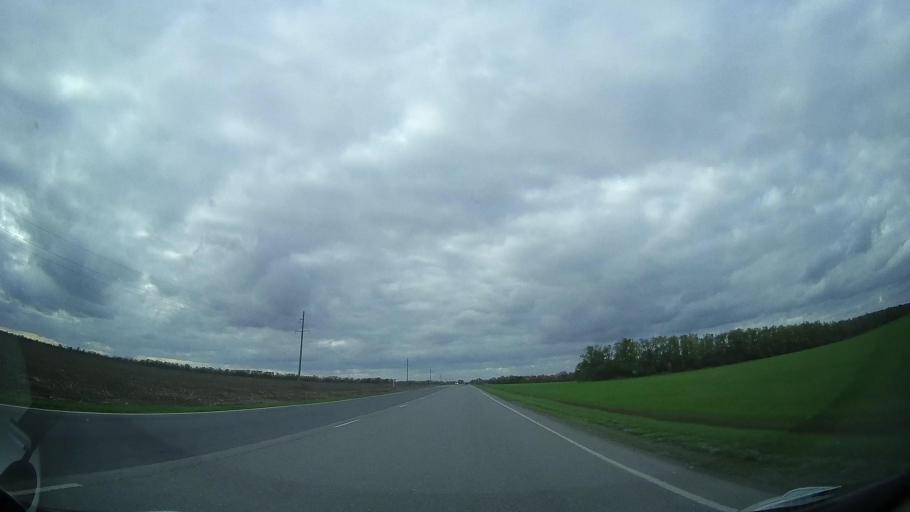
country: RU
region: Rostov
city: Mechetinskaya
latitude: 46.7900
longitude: 40.3992
